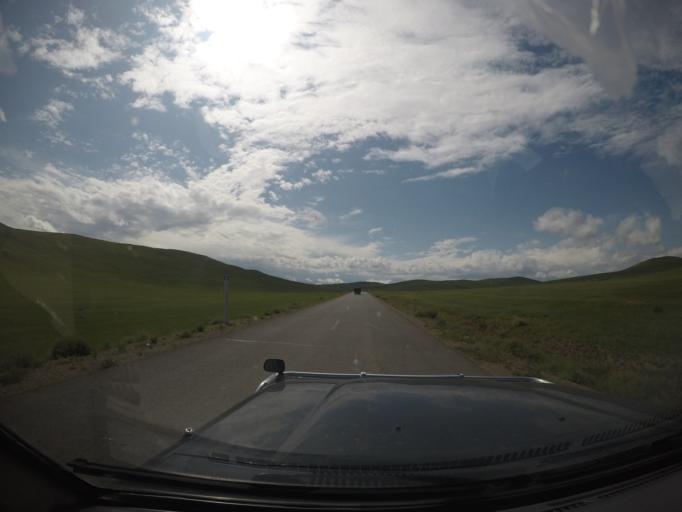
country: MN
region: Hentiy
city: Bayanbulag
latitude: 47.4552
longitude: 109.8087
